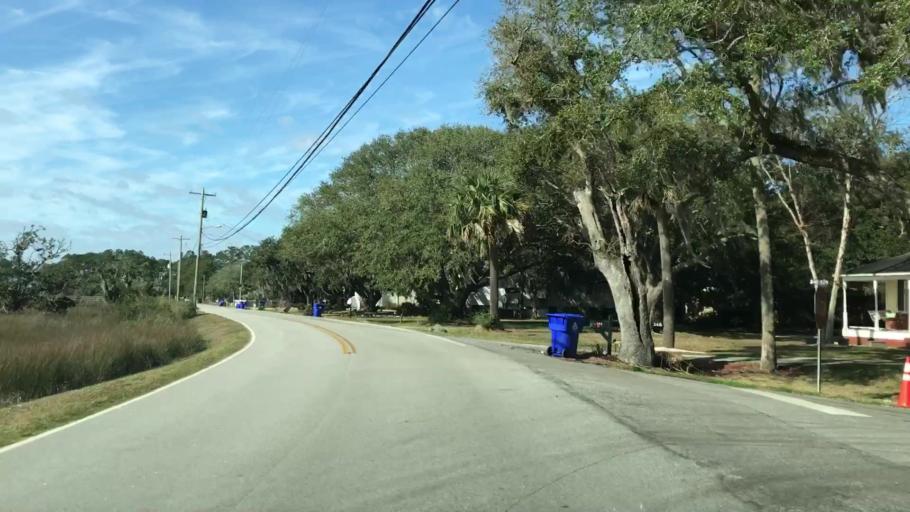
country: US
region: South Carolina
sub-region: Charleston County
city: Charleston
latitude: 32.7736
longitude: -80.0114
